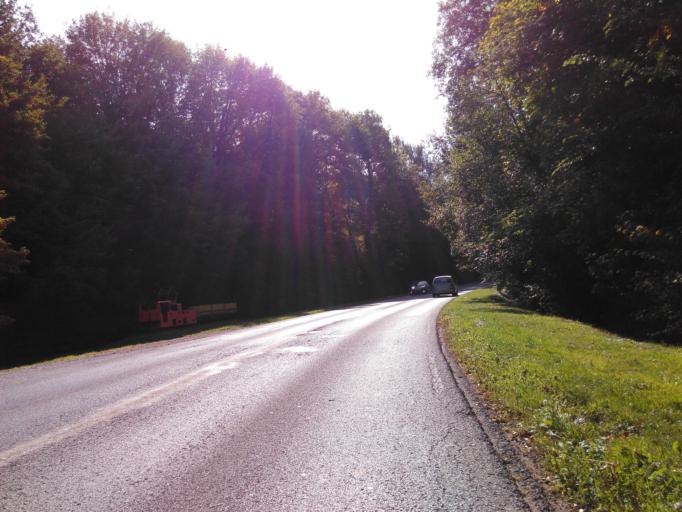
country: FR
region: Lorraine
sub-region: Departement de la Moselle
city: Ottange
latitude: 49.4444
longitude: 6.0248
